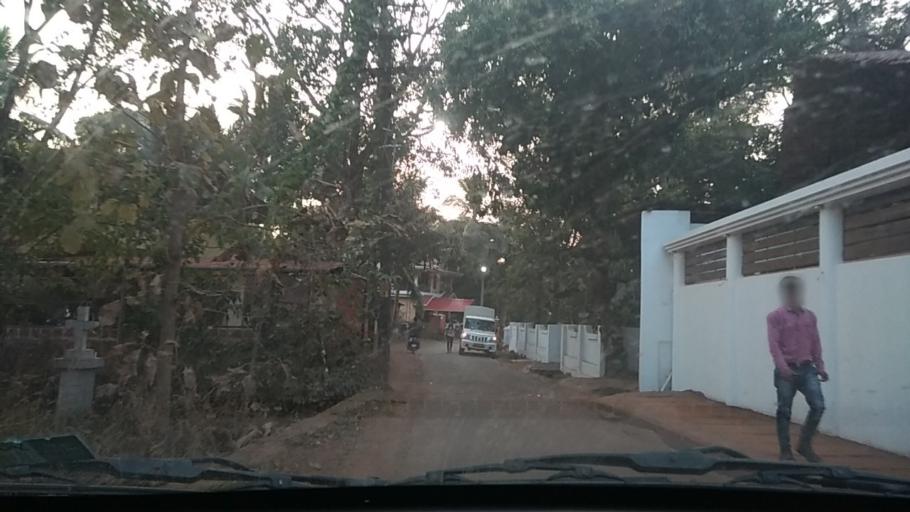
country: IN
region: Goa
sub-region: South Goa
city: Sancoale
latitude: 15.3479
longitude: 73.9346
